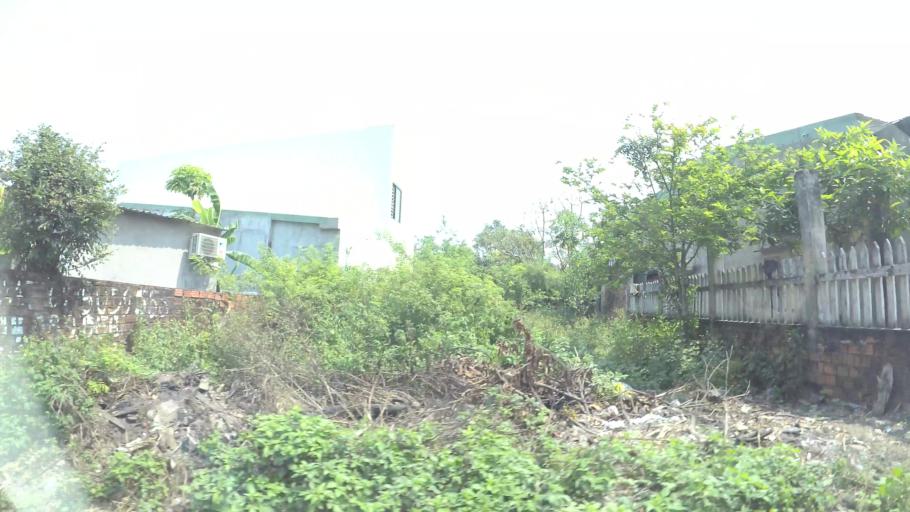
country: VN
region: Da Nang
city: Ngu Hanh Son
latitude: 16.0080
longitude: 108.2547
